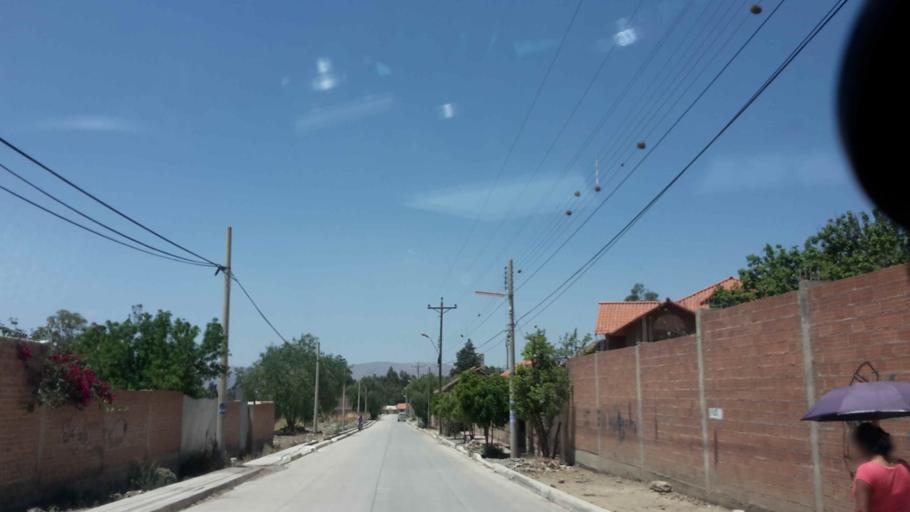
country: BO
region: Cochabamba
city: Cochabamba
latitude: -17.3530
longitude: -66.2068
